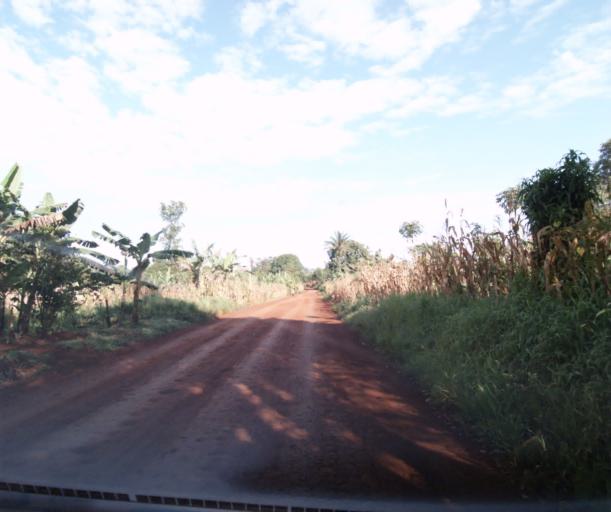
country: CM
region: West
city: Mbouda
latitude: 5.6221
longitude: 10.3272
